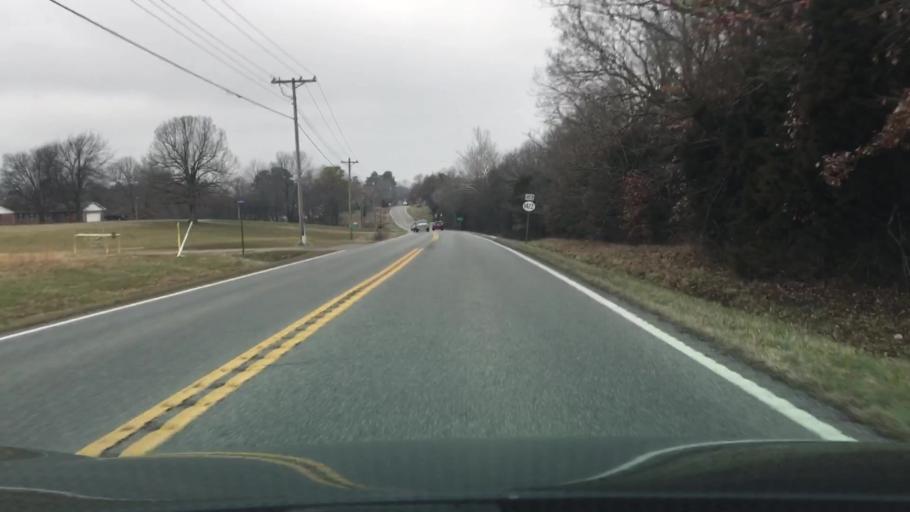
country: US
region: Kentucky
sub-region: Marshall County
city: Calvert City
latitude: 36.9558
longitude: -88.3721
